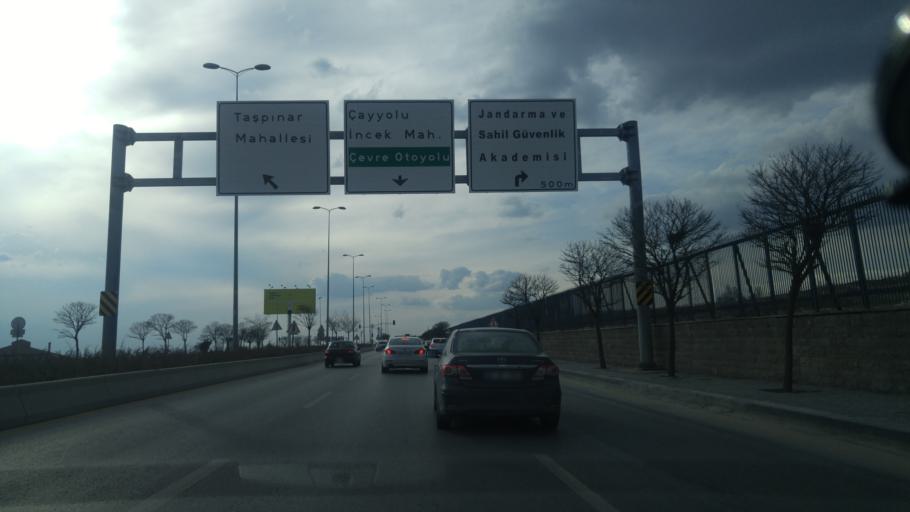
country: TR
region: Ankara
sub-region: Goelbasi
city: Golbasi
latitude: 39.8357
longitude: 32.7672
